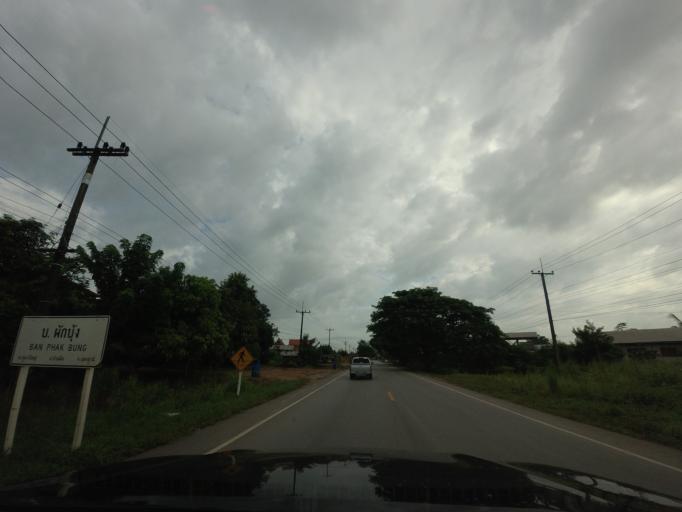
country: TH
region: Changwat Udon Thani
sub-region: Amphoe Ban Phue
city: Ban Phue
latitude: 17.7416
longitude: 102.3982
